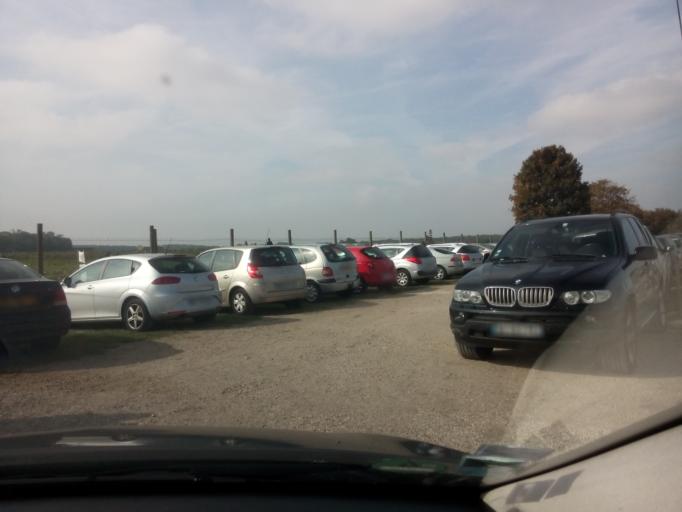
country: FR
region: Ile-de-France
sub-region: Departement des Yvelines
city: Jouy-en-Josas
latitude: 48.7523
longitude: 2.1631
